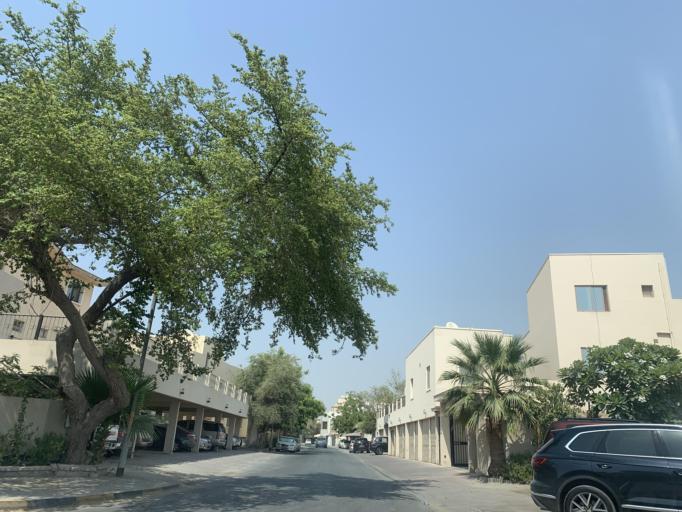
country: BH
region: Manama
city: Jidd Hafs
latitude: 26.1995
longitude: 50.5284
